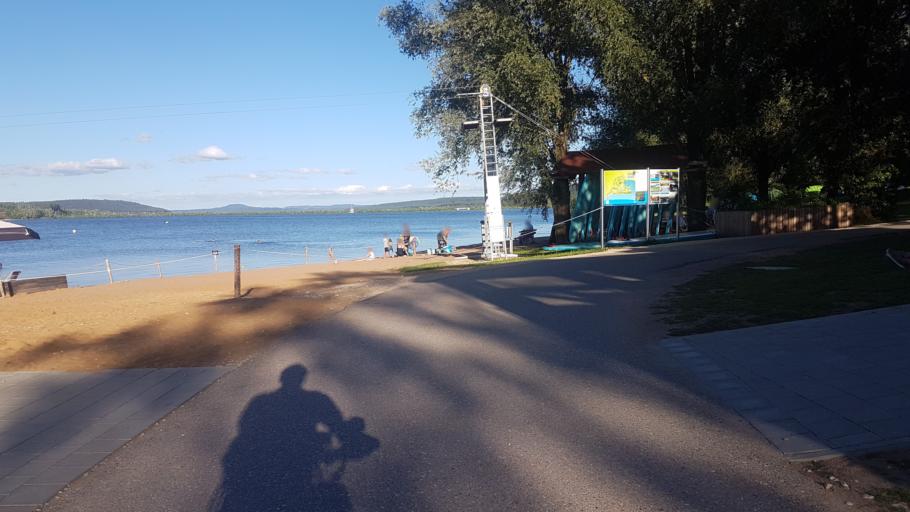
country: DE
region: Bavaria
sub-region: Regierungsbezirk Mittelfranken
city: Absberg
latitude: 49.1382
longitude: 10.8776
